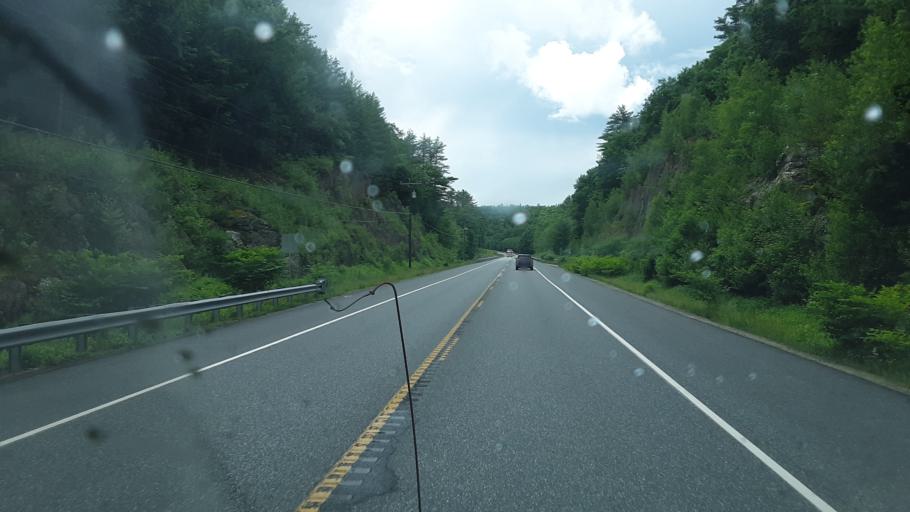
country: US
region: New Hampshire
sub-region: Cheshire County
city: Keene
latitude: 42.9684
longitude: -72.2319
